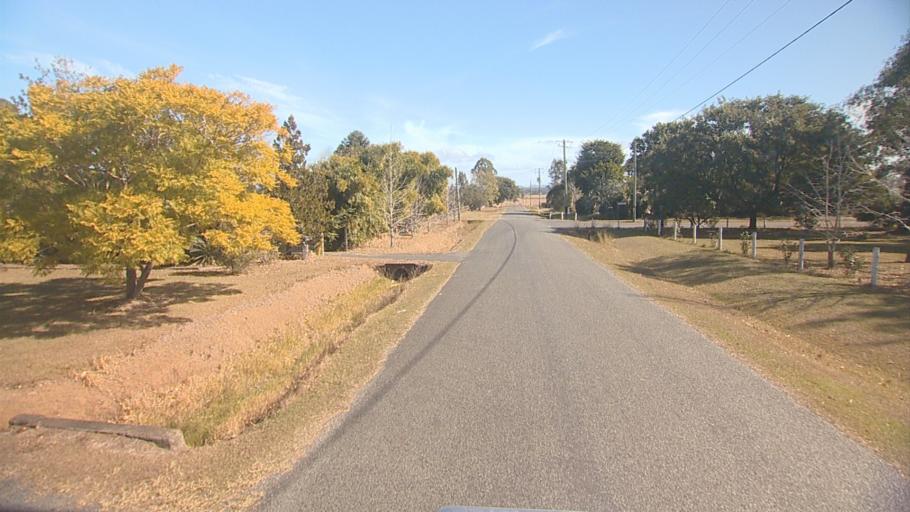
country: AU
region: Queensland
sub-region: Logan
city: Cedar Vale
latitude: -27.8679
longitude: 152.9686
